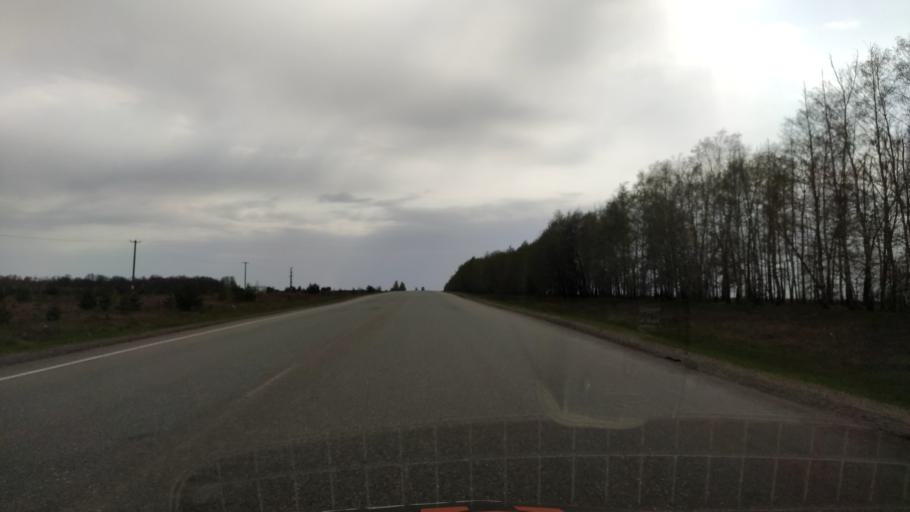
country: RU
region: Kursk
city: Gorshechnoye
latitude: 51.4586
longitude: 37.9223
